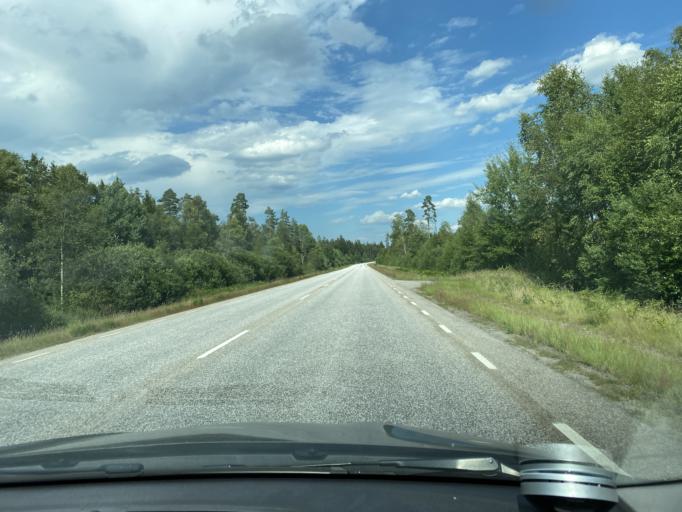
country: SE
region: Kronoberg
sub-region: Markaryds Kommun
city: Markaryd
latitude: 56.4218
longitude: 13.5505
